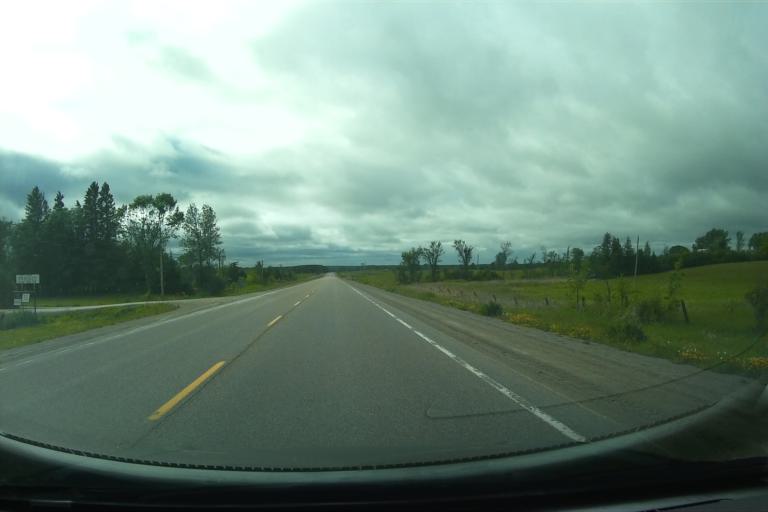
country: CA
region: Ontario
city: Renfrew
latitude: 45.5239
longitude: -76.9576
